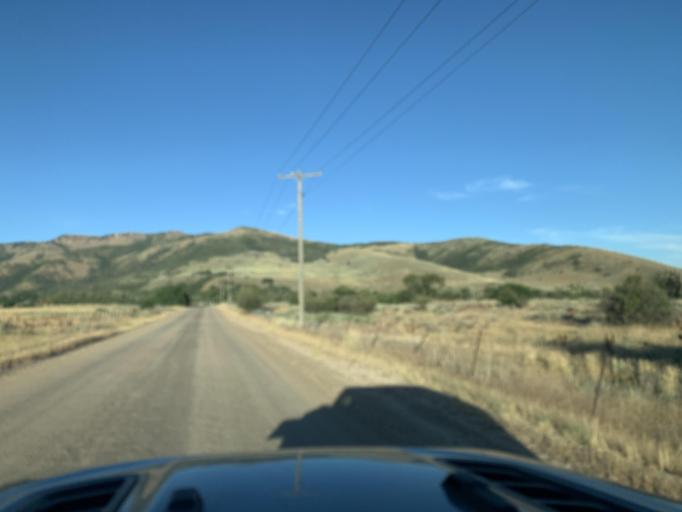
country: US
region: Utah
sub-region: Weber County
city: Wolf Creek
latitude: 41.2931
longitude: -111.7610
